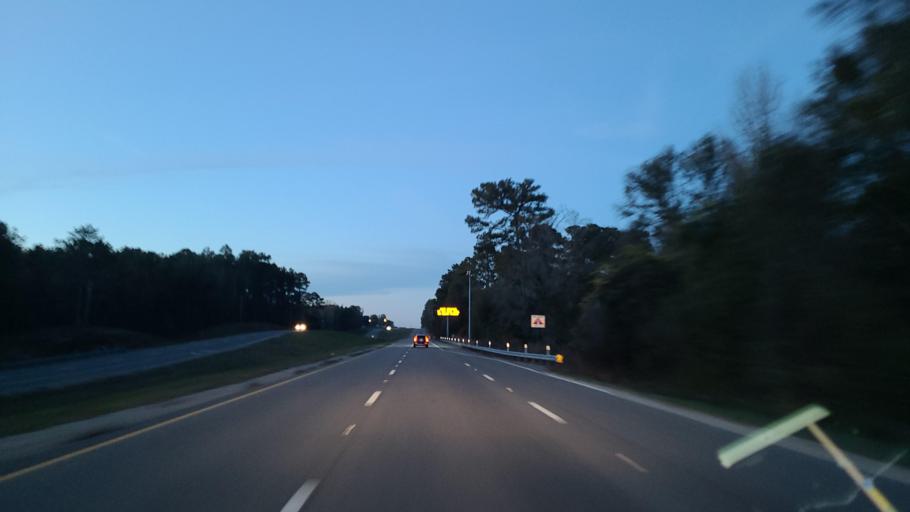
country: US
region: Mississippi
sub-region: Forrest County
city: Hattiesburg
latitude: 31.2133
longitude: -89.2624
